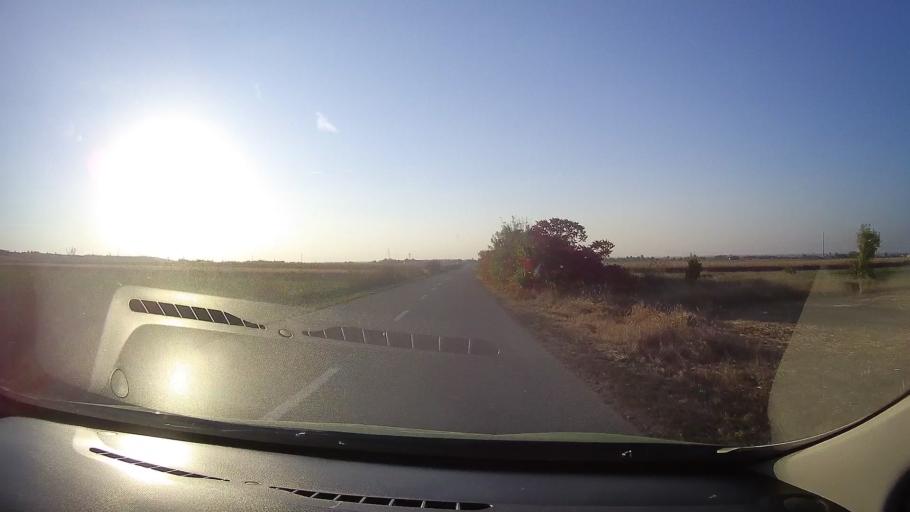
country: RO
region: Bihor
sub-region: Comuna Paleu
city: Paleu
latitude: 47.1613
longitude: 21.9666
